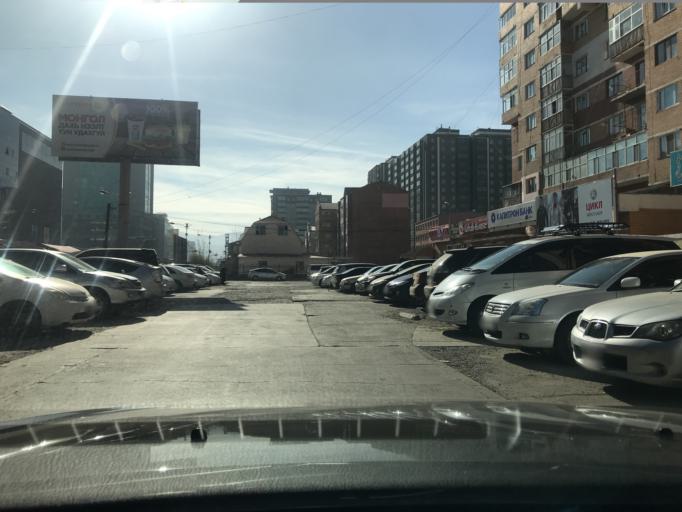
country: MN
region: Ulaanbaatar
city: Ulaanbaatar
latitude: 47.9115
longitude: 106.9431
